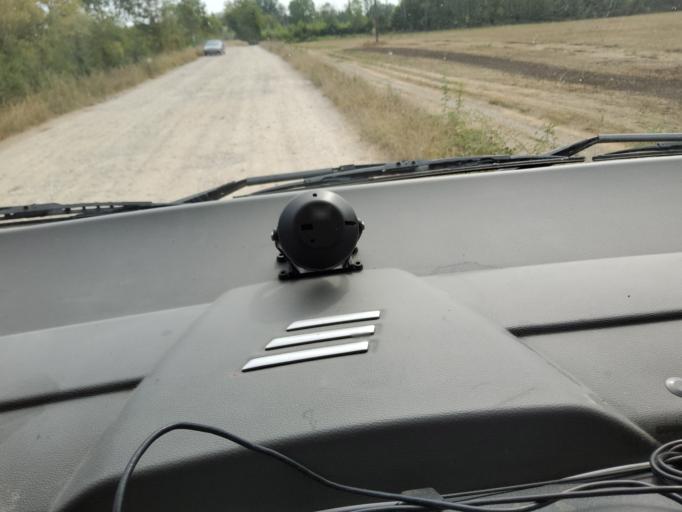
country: FR
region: Franche-Comte
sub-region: Departement du Jura
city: Choisey
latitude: 47.0136
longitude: 5.4882
